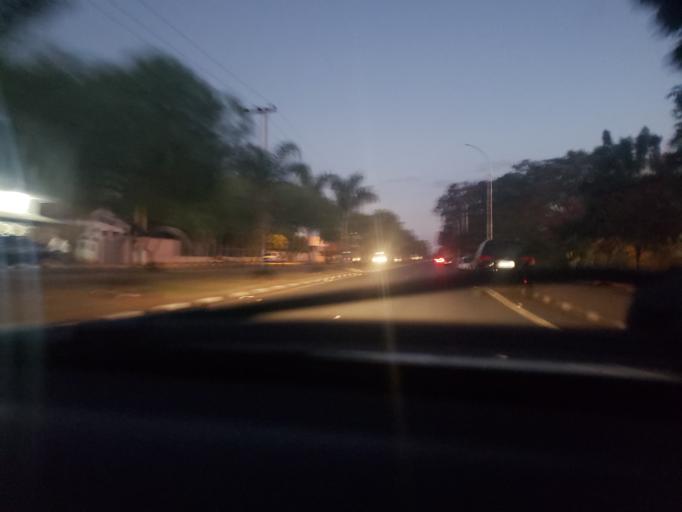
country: BR
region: Sao Paulo
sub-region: Conchal
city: Conchal
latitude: -22.2897
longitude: -47.1335
